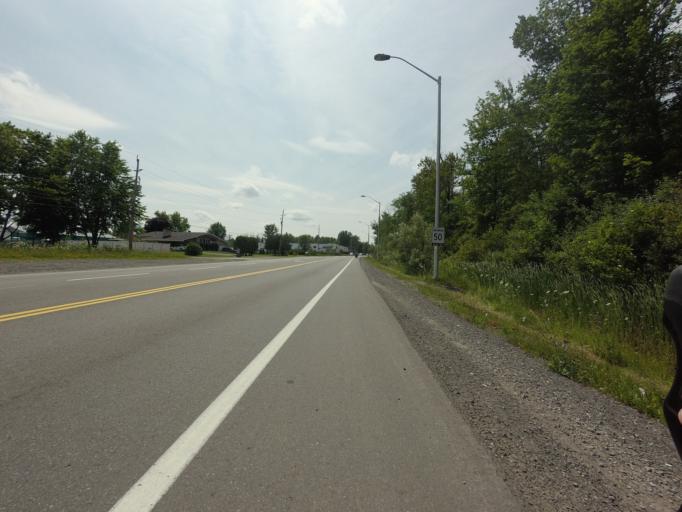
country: CA
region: Ontario
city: Ottawa
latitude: 45.3200
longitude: -75.6246
